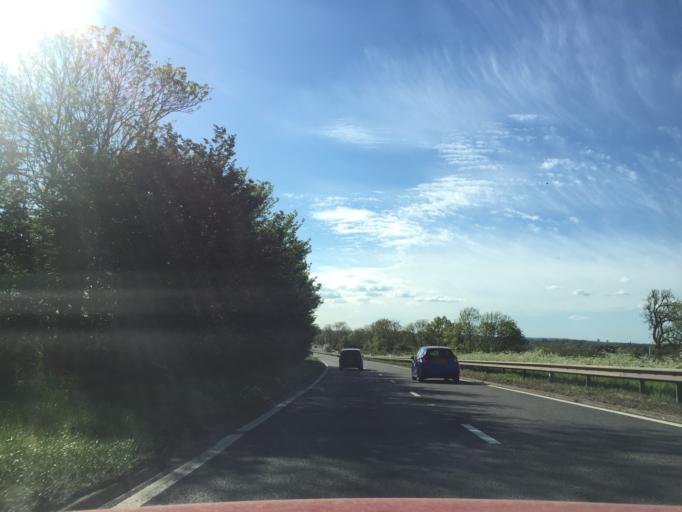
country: GB
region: England
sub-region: Warwickshire
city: Wolston
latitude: 52.3613
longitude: -1.4110
